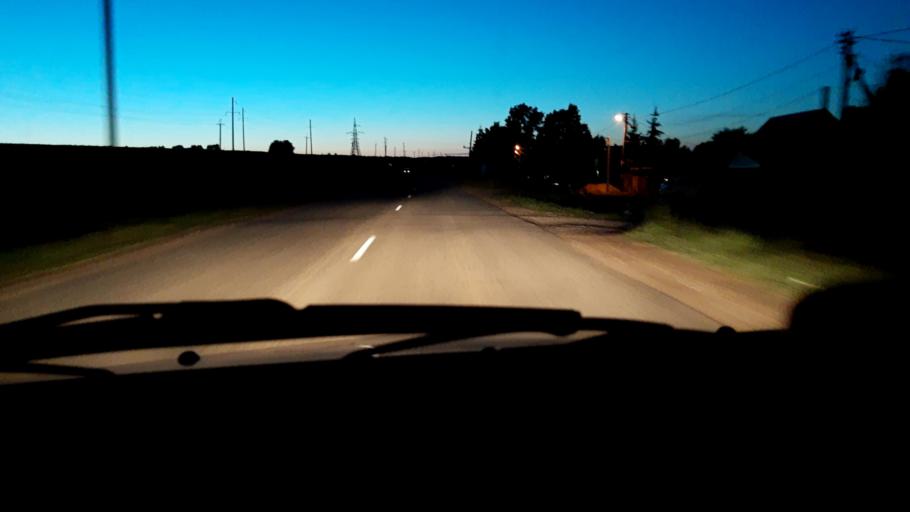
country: RU
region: Bashkortostan
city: Mikhaylovka
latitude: 54.9001
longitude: 55.8750
